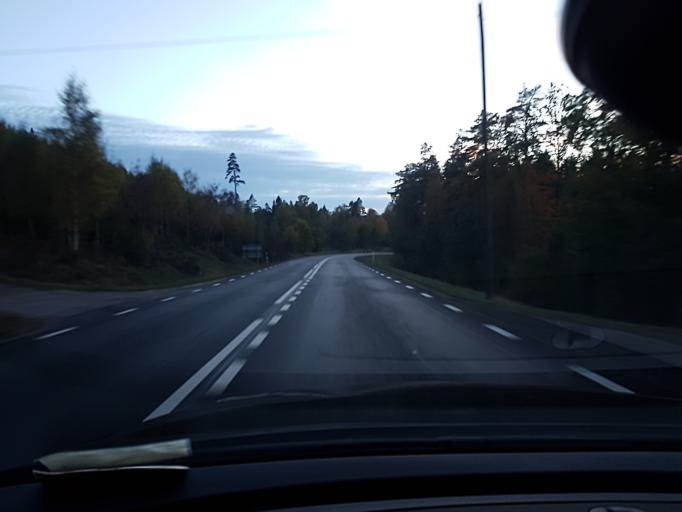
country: SE
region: Halland
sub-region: Laholms Kommun
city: Veinge
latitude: 56.7208
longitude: 13.1509
